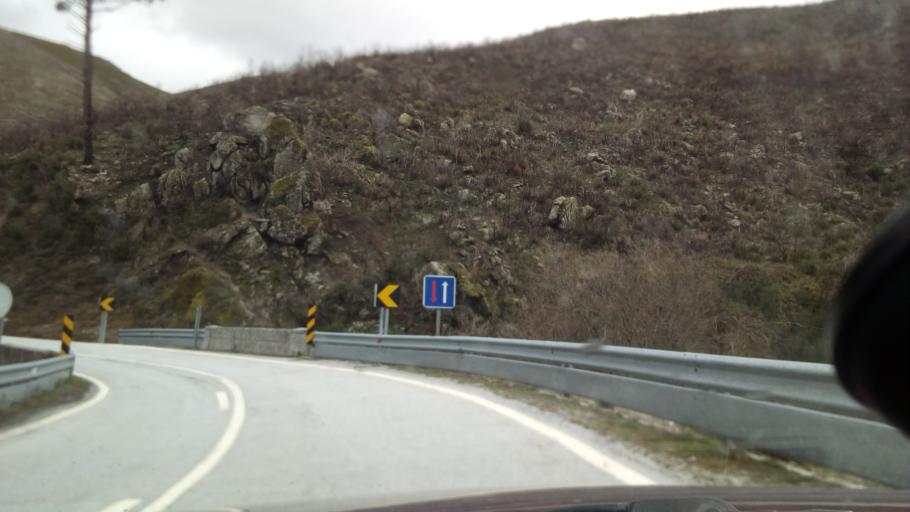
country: PT
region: Guarda
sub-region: Manteigas
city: Manteigas
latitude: 40.4500
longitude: -7.5871
